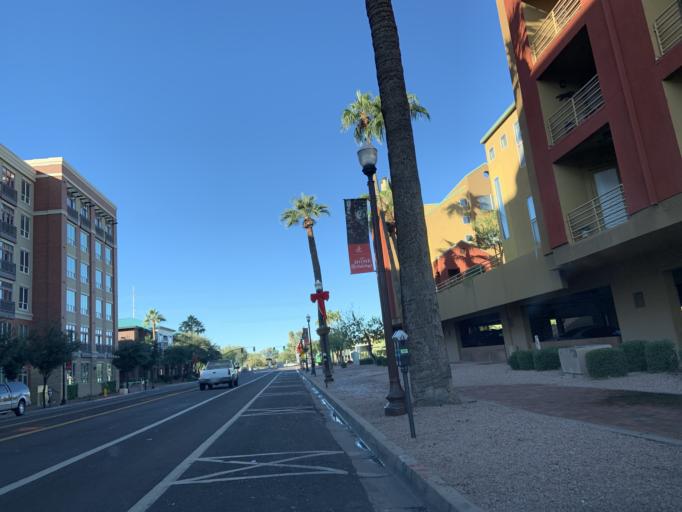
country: US
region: Arizona
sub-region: Maricopa County
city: Tempe Junction
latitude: 33.4255
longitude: -111.9416
